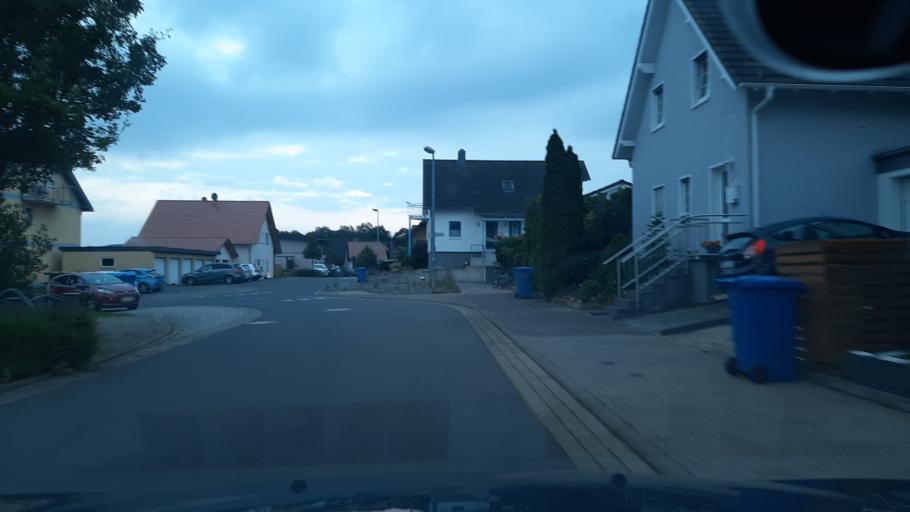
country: DE
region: North Rhine-Westphalia
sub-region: Regierungsbezirk Koln
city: Mechernich
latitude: 50.5972
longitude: 6.6611
